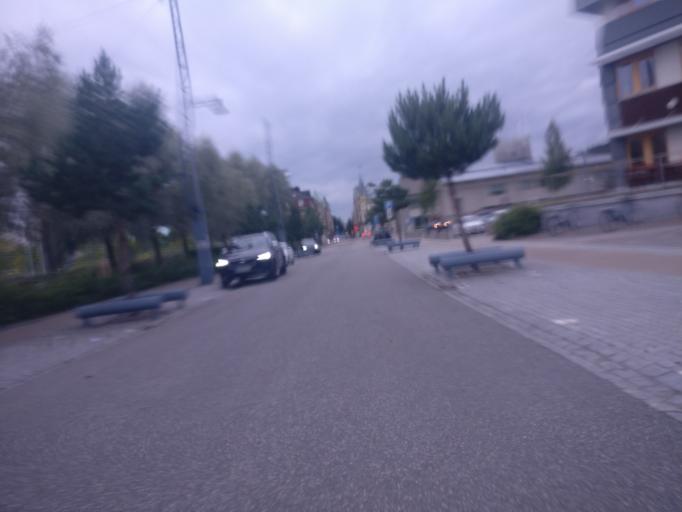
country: SE
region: Vaesternorrland
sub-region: Sundsvalls Kommun
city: Sundsvall
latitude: 62.3900
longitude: 17.3177
